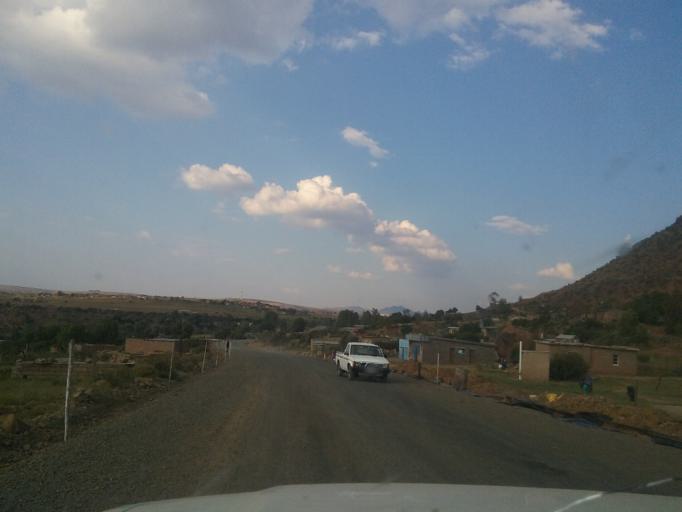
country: LS
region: Quthing
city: Quthing
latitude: -30.3958
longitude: 27.6145
